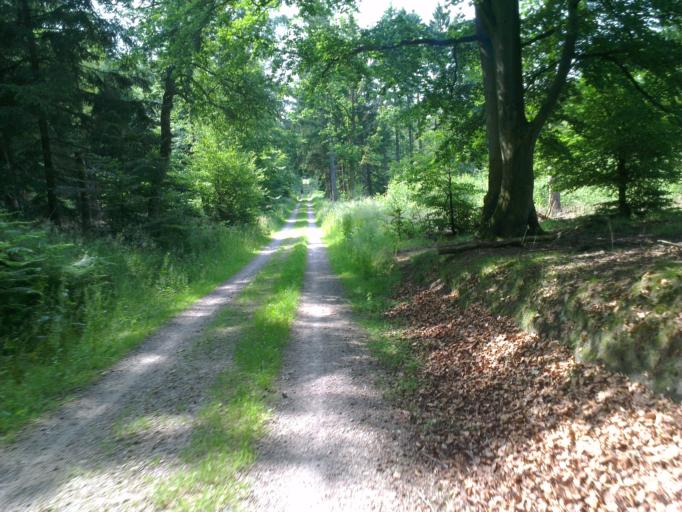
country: DK
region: Capital Region
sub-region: Allerod Kommune
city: Lillerod
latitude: 55.9056
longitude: 12.3570
